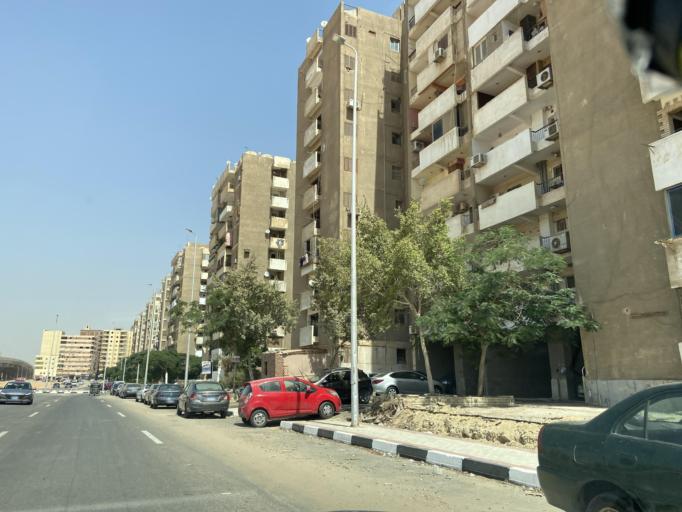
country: EG
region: Muhafazat al Qahirah
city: Cairo
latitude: 30.0594
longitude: 31.3777
